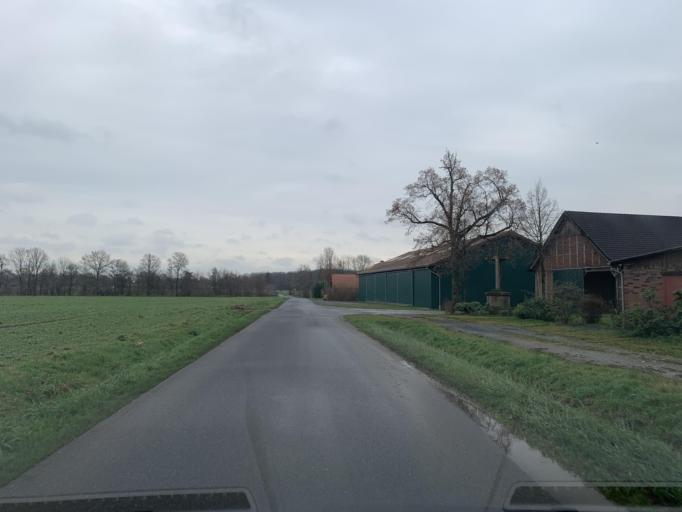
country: DE
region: North Rhine-Westphalia
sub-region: Regierungsbezirk Munster
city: Senden
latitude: 51.8961
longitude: 7.5600
